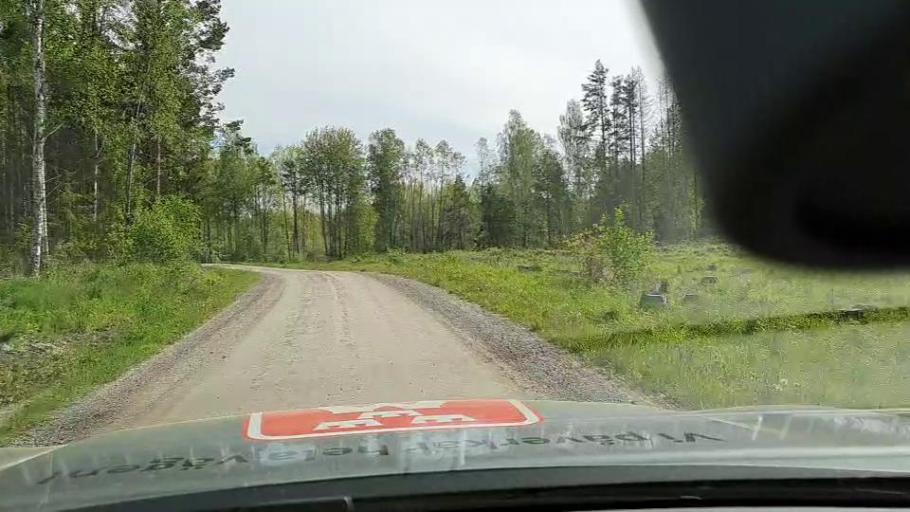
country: SE
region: Soedermanland
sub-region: Eskilstuna Kommun
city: Arla
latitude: 59.2622
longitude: 16.8123
